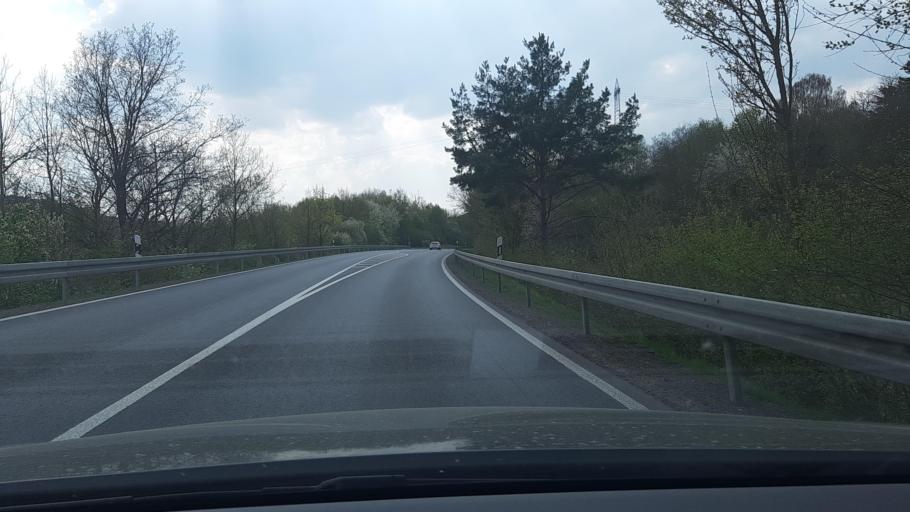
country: DE
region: Hesse
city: Staufenberg
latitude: 50.6533
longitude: 8.7289
